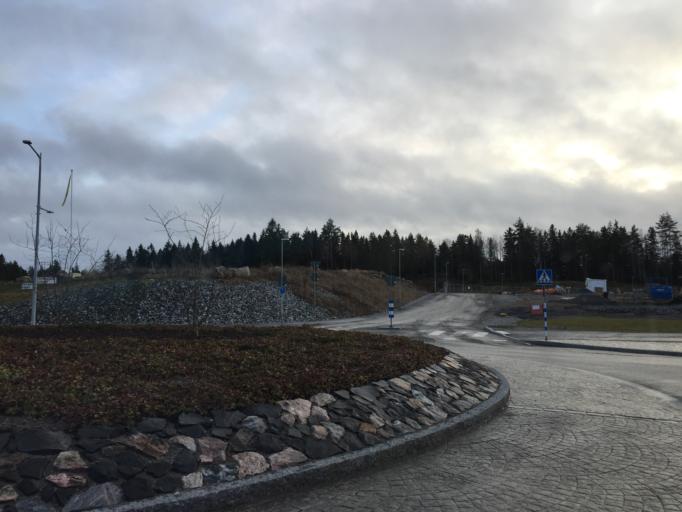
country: SE
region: Stockholm
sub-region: Sodertalje Kommun
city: Soedertaelje
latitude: 59.2195
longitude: 17.6487
